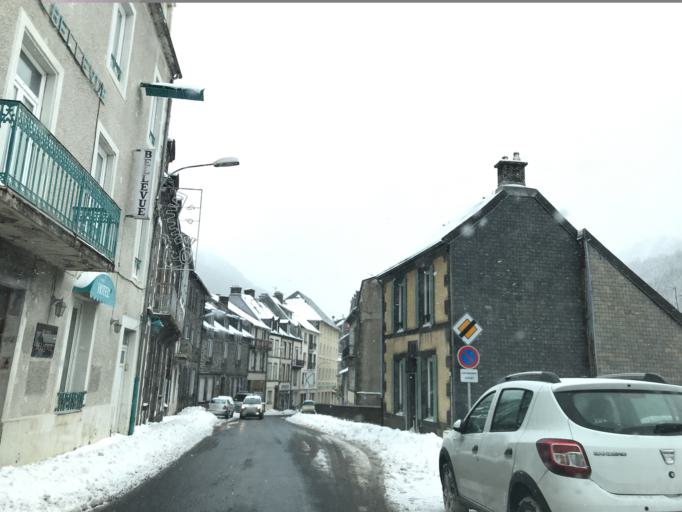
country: FR
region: Auvergne
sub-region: Departement du Puy-de-Dome
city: Mont-Dore
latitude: 45.5763
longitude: 2.8100
